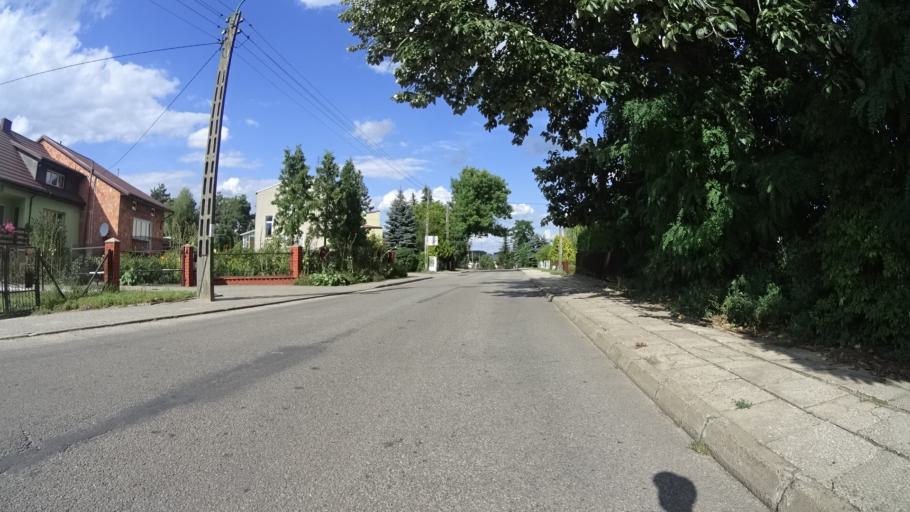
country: PL
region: Masovian Voivodeship
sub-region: Powiat grojecki
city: Mogielnica
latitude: 51.6879
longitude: 20.7195
